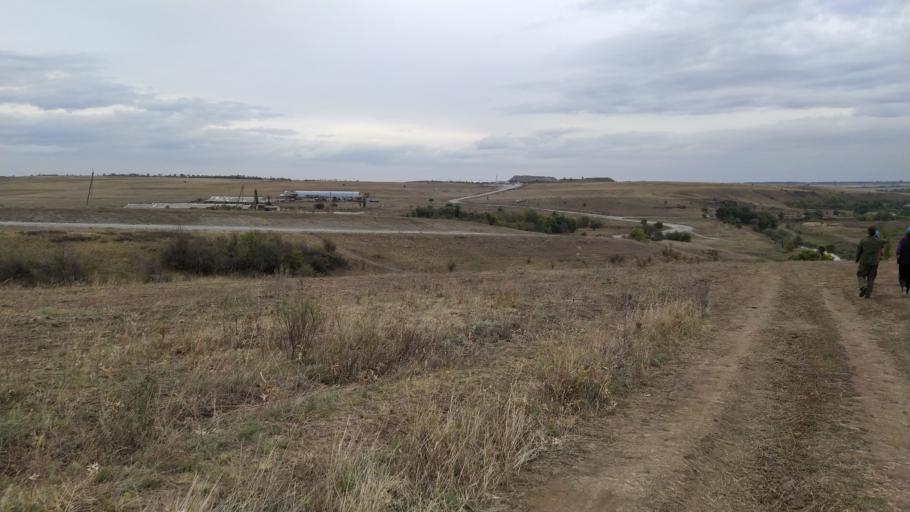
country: RU
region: Rostov
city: Gornyy
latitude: 47.8905
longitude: 40.2442
